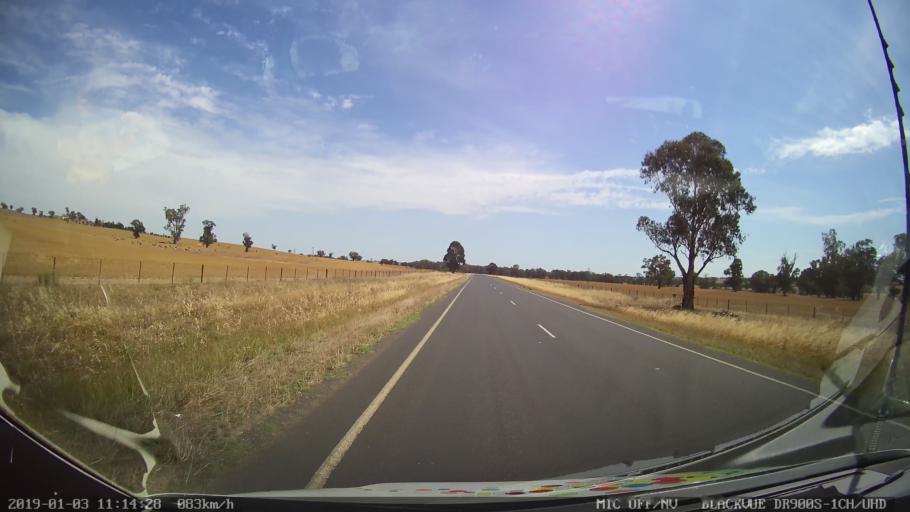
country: AU
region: New South Wales
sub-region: Young
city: Young
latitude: -34.1758
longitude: 148.2609
